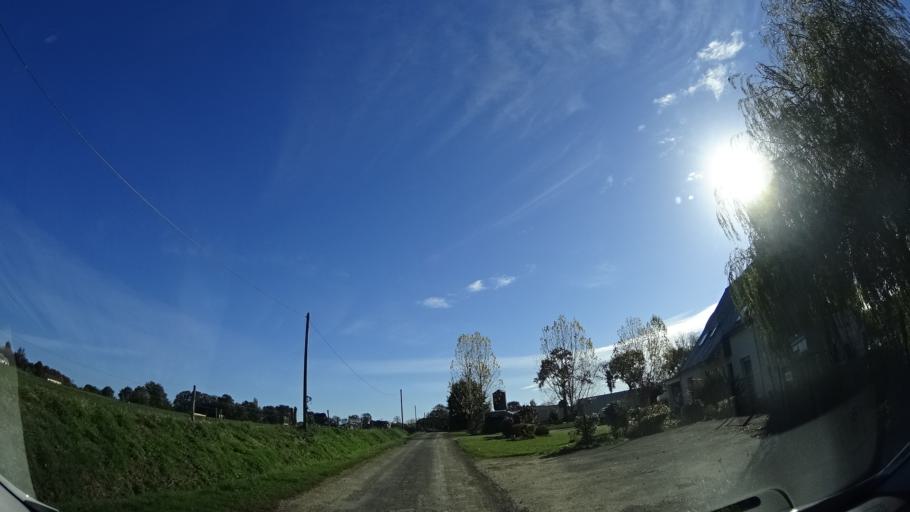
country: FR
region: Brittany
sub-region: Departement d'Ille-et-Vilaine
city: La Meziere
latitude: 48.2062
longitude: -1.7568
